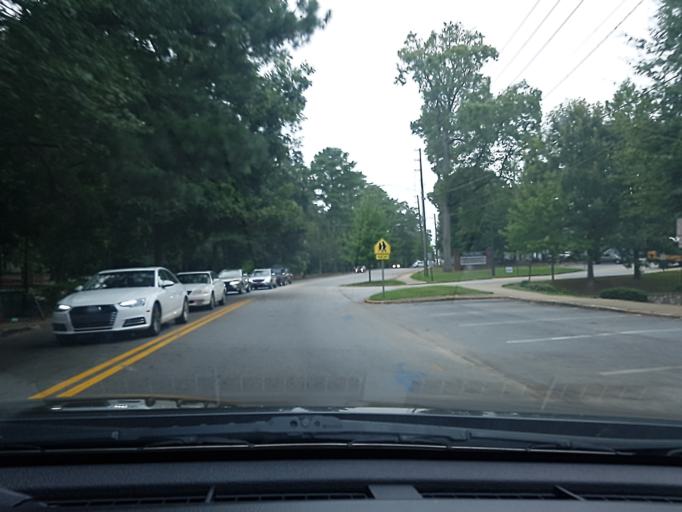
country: US
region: Georgia
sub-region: DeKalb County
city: North Decatur
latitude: 33.7922
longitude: -84.3152
